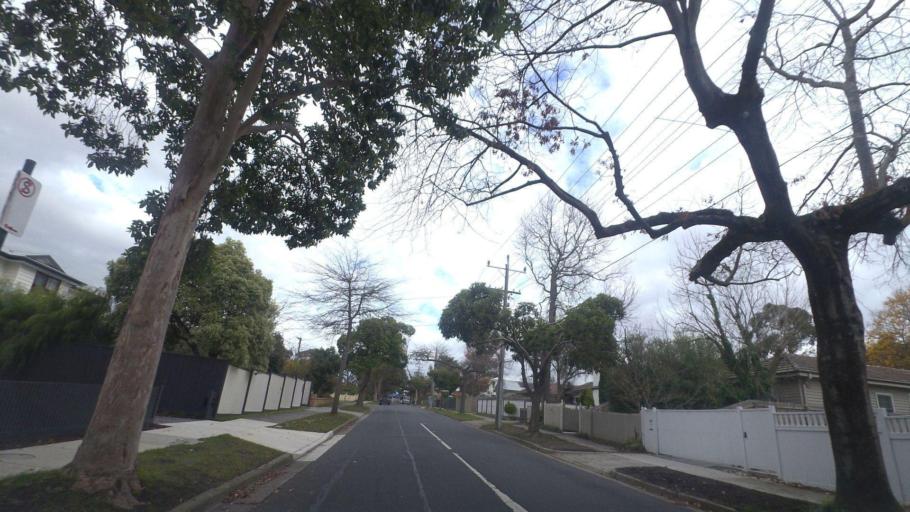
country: AU
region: Victoria
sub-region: Whitehorse
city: Nunawading
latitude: -37.8155
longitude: 145.1637
